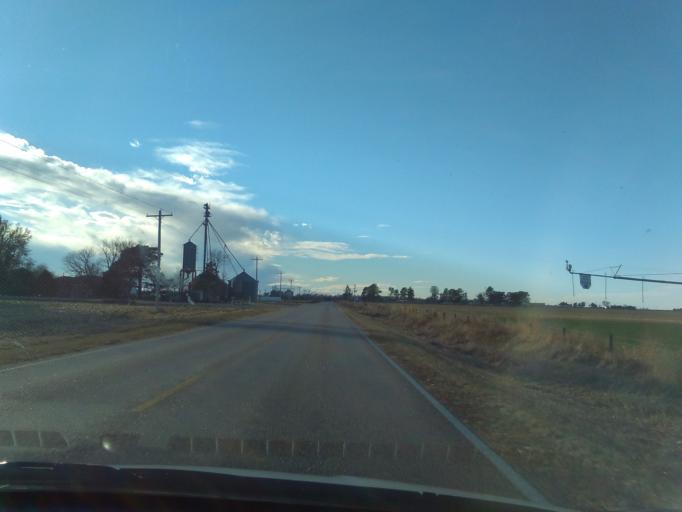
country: US
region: Nebraska
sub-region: Phelps County
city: Holdrege
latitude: 40.3649
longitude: -99.1452
